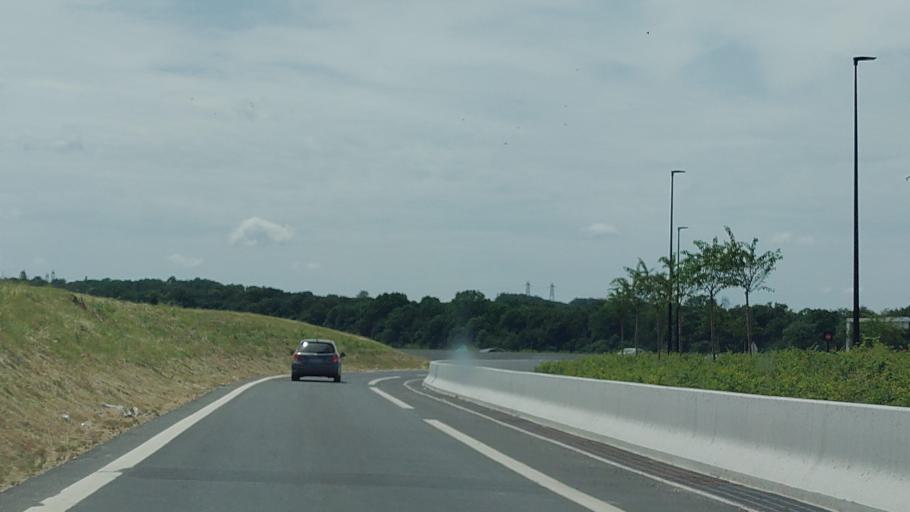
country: FR
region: Ile-de-France
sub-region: Departement de Seine-et-Marne
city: Villevaude
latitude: 48.9437
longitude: 2.6552
